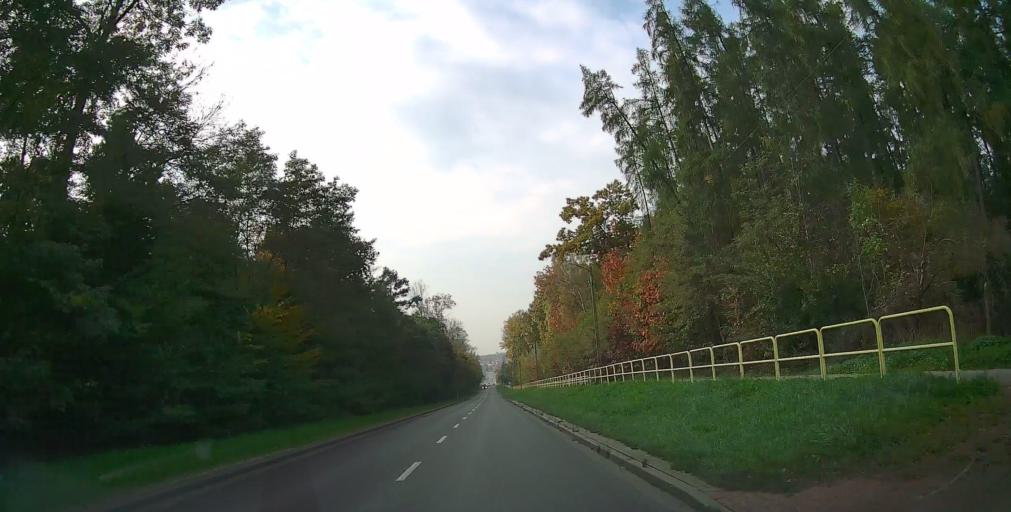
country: PL
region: Masovian Voivodeship
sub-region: Powiat grojecki
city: Mogielnica
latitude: 51.6997
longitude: 20.7308
